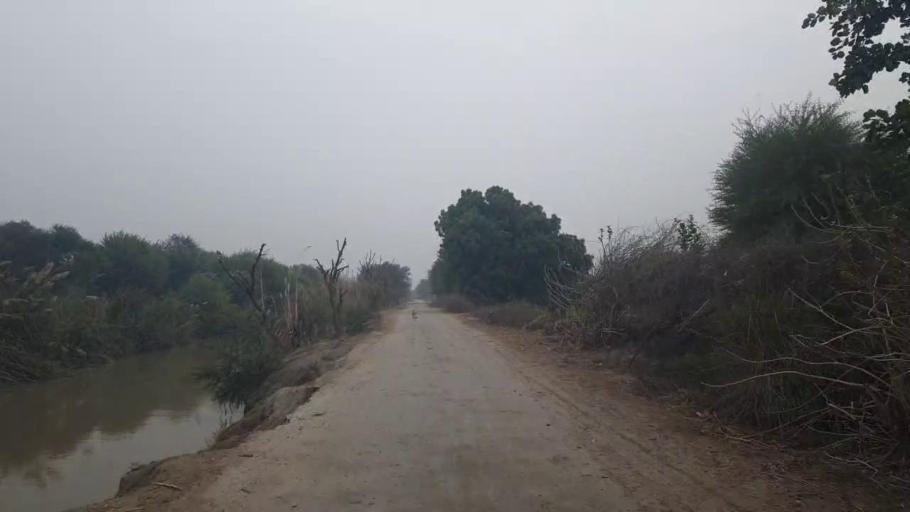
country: PK
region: Sindh
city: Tando Adam
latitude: 25.7474
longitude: 68.7054
